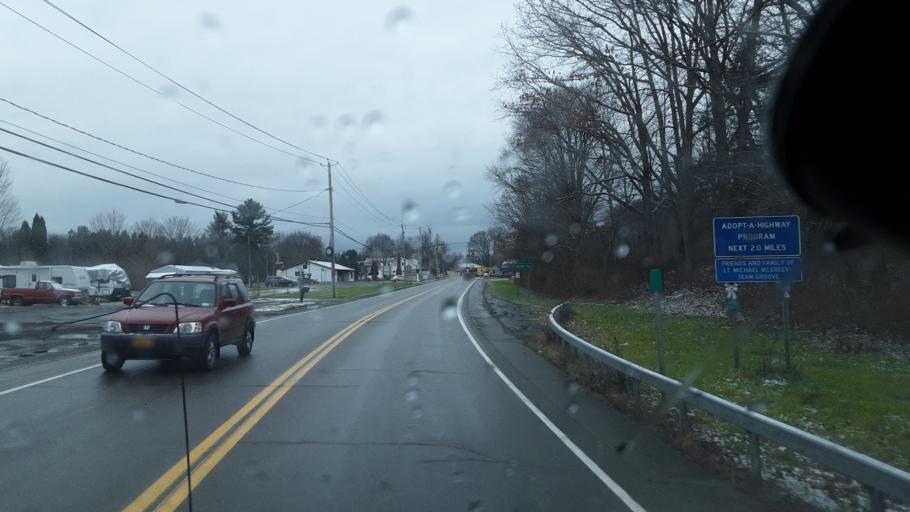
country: US
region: New York
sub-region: Cattaraugus County
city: Westons Mills
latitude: 42.0570
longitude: -78.3707
